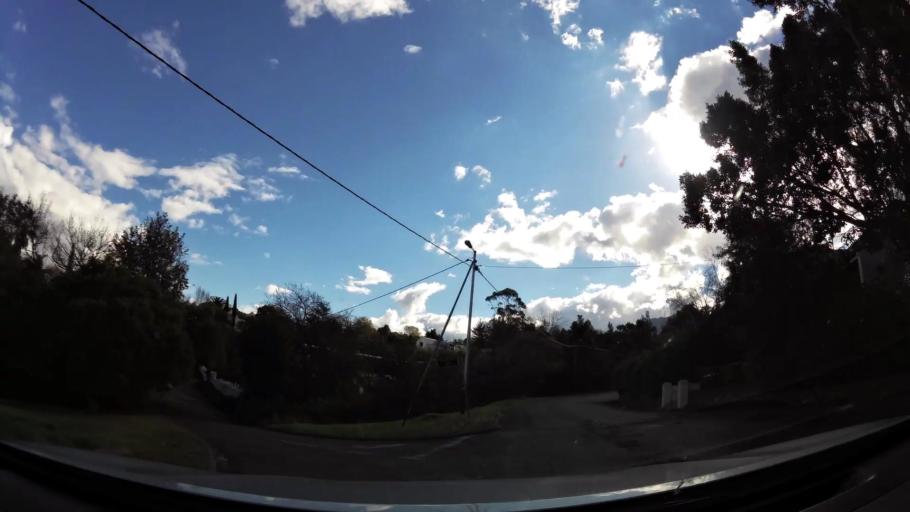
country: ZA
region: Western Cape
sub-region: Overberg District Municipality
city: Swellendam
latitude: -34.0170
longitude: 20.4440
